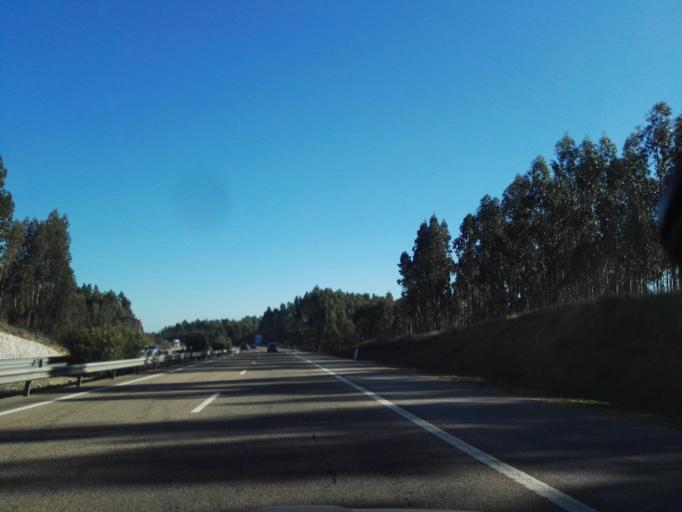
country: PT
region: Santarem
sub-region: Chamusca
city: Vila Nova da Barquinha
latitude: 39.4862
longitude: -8.4170
